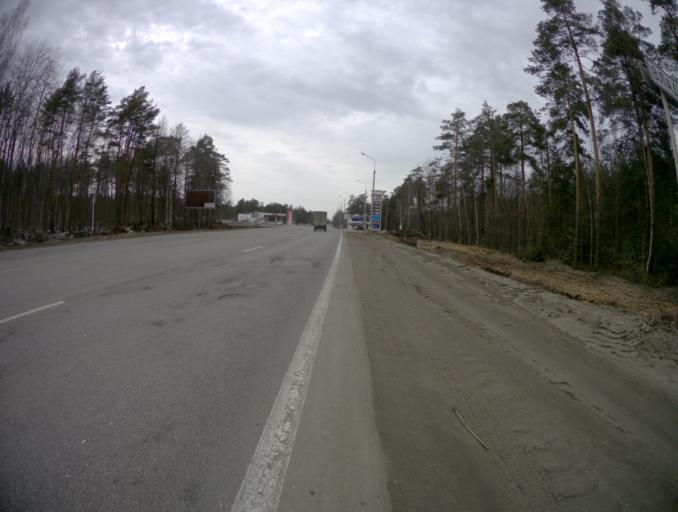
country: RU
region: Vladimir
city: Kommunar
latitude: 56.0952
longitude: 40.4482
